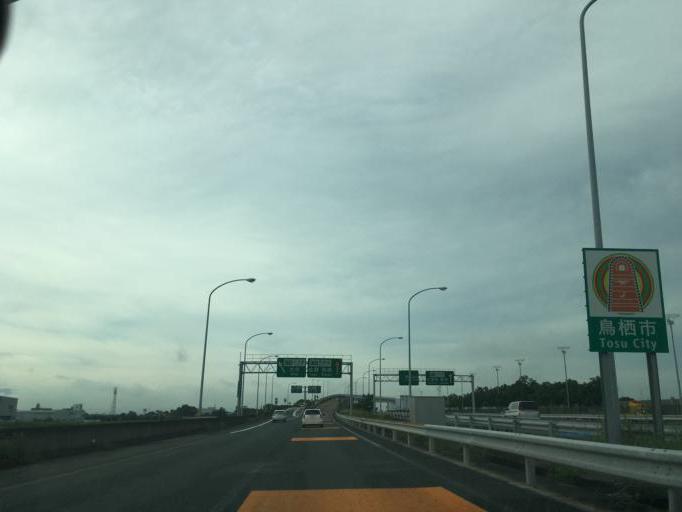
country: JP
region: Saga Prefecture
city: Tosu
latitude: 33.4028
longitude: 130.5382
